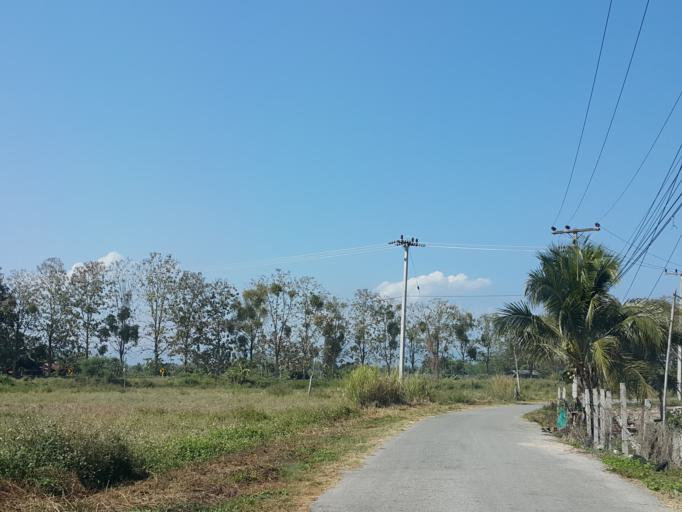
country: TH
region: Chiang Mai
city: Mae Taeng
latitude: 19.0345
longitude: 98.9817
